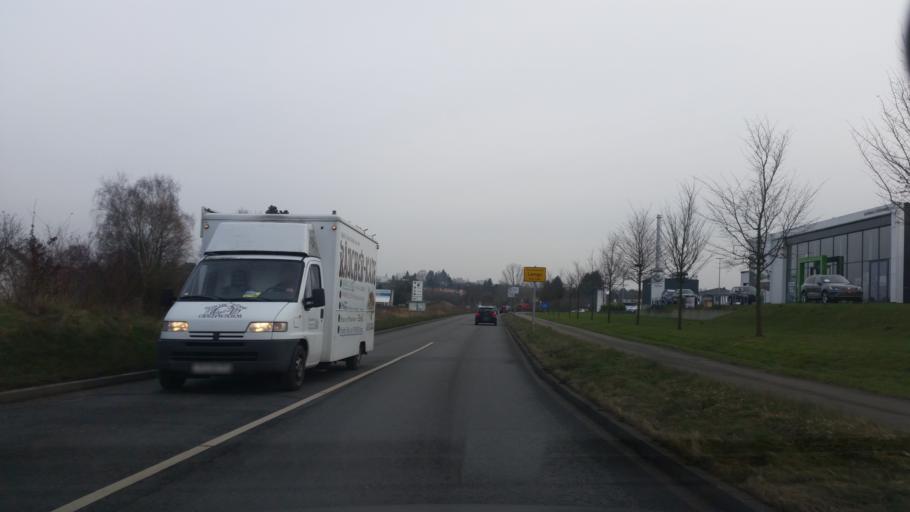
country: DE
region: North Rhine-Westphalia
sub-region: Regierungsbezirk Detmold
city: Lemgo
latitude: 52.0212
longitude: 8.8762
